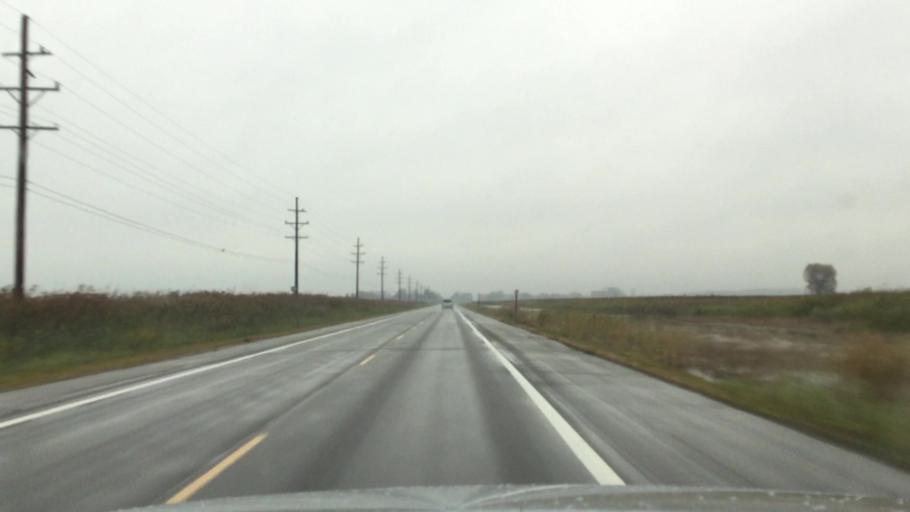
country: US
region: Michigan
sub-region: Saint Clair County
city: Pearl Beach
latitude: 42.6425
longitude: -82.6172
